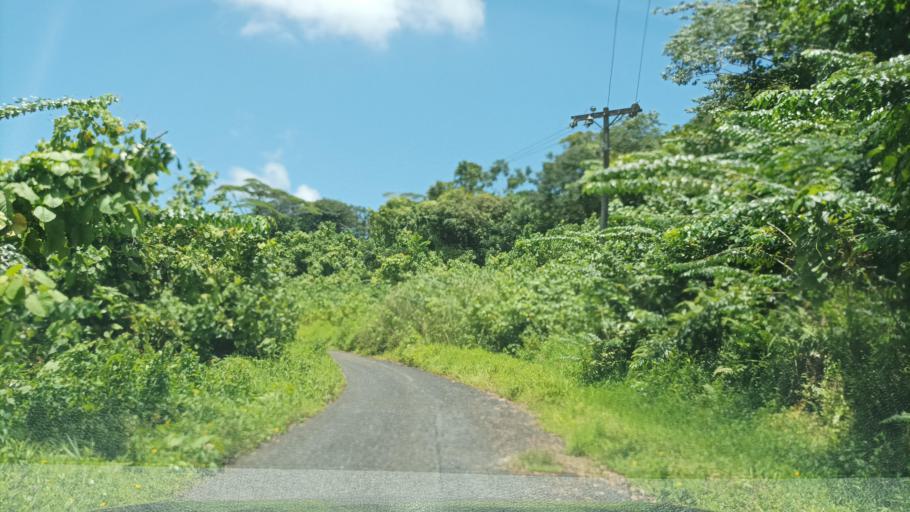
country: FM
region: Pohnpei
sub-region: Madolenihm Municipality
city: Madolenihm Municipality Government
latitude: 6.8426
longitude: 158.3115
